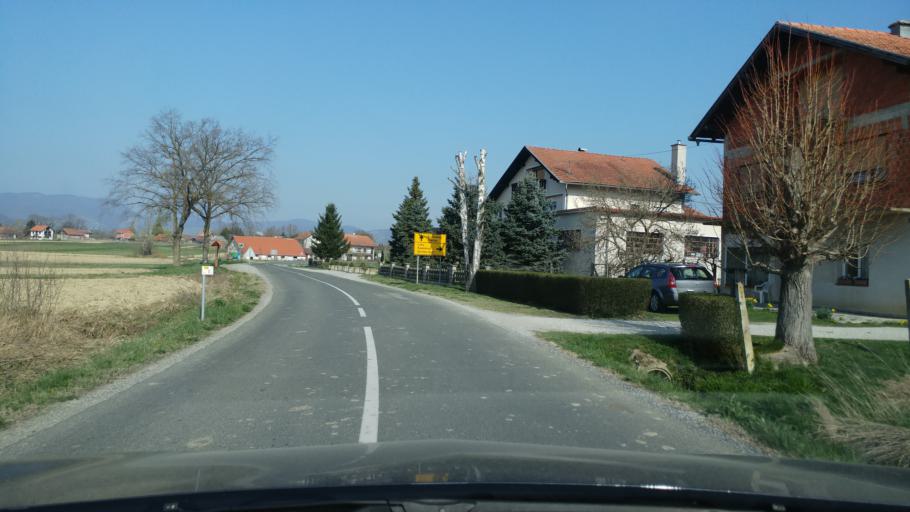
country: HR
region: Zagrebacka
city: Pojatno
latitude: 45.9747
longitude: 15.7369
